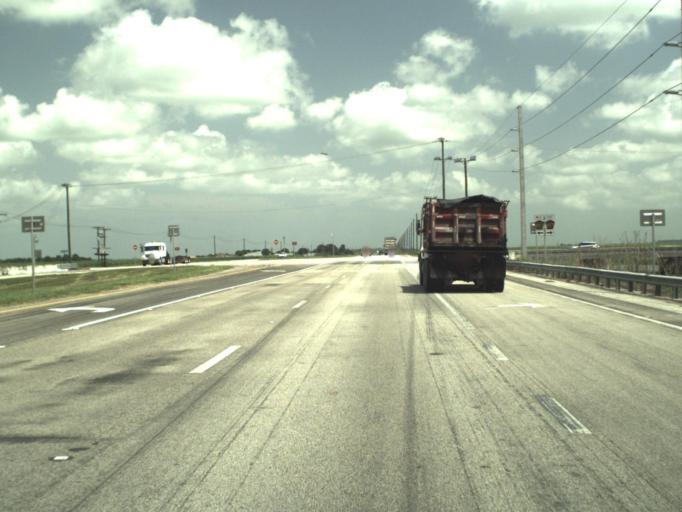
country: US
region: Florida
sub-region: Palm Beach County
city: South Bay
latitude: 26.6088
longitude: -80.7115
